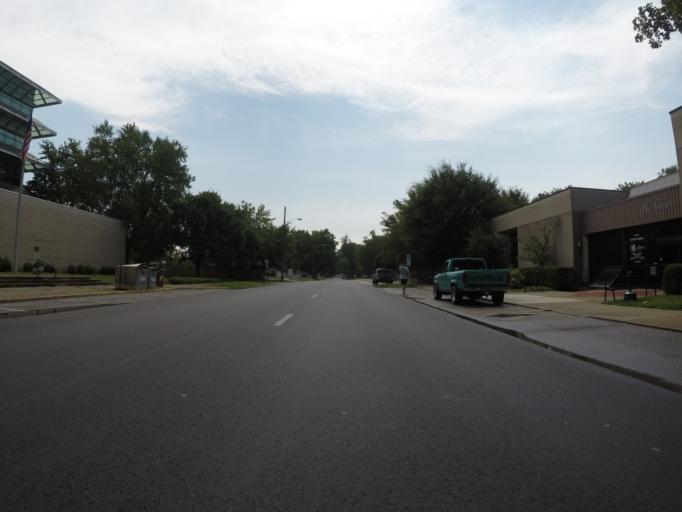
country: US
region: Kentucky
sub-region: Boyd County
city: Ashland
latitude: 38.4759
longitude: -82.6392
